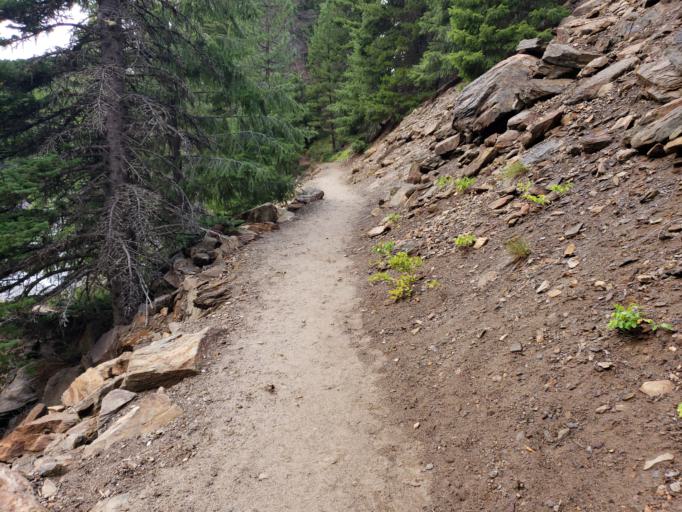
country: US
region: Washington
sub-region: Chelan County
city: Leavenworth
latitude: 47.6067
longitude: -120.8869
